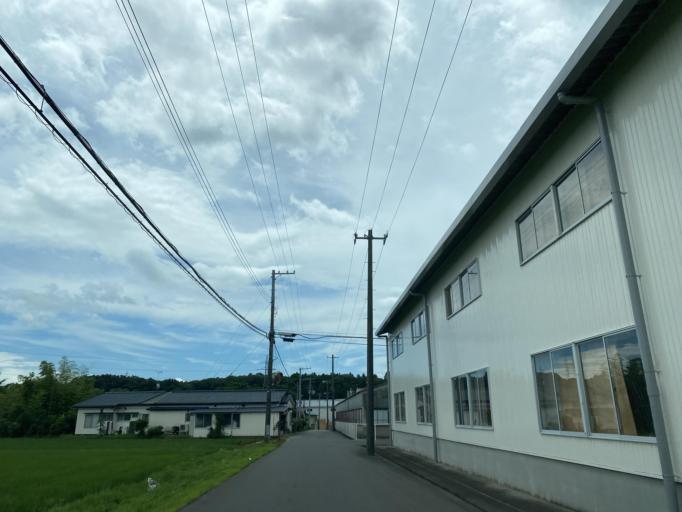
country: JP
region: Fukushima
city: Koriyama
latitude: 37.3622
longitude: 140.3465
